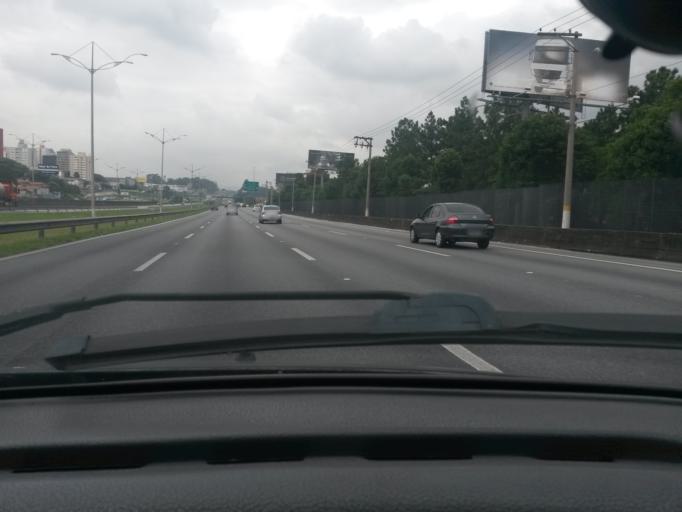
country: BR
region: Sao Paulo
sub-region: Sao Bernardo Do Campo
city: Sao Bernardo do Campo
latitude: -23.6618
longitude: -46.5755
